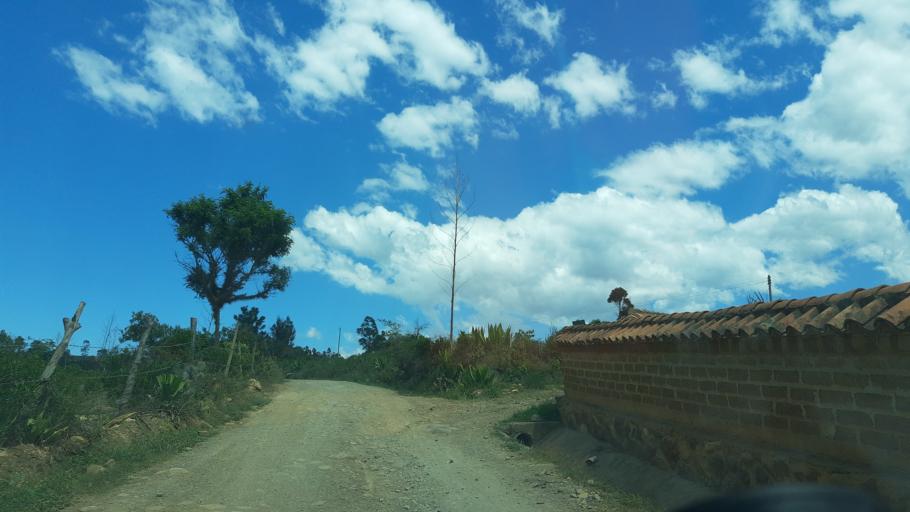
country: CO
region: Boyaca
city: Villa de Leiva
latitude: 5.6717
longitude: -73.5714
